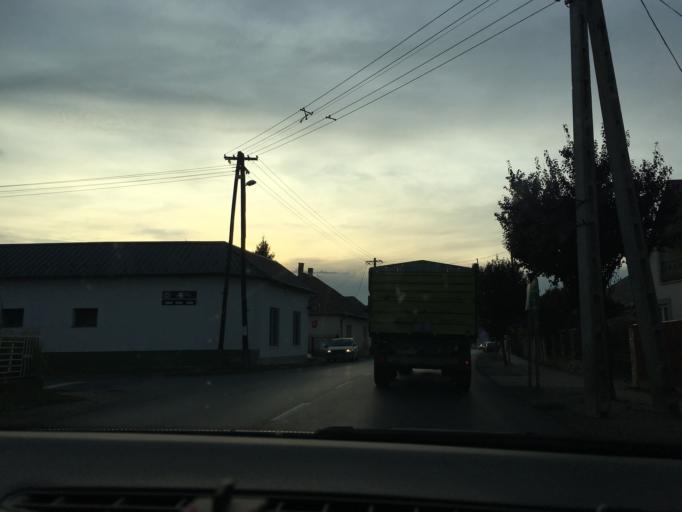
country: HU
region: Szabolcs-Szatmar-Bereg
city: Kallosemjen
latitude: 47.8589
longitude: 21.9311
